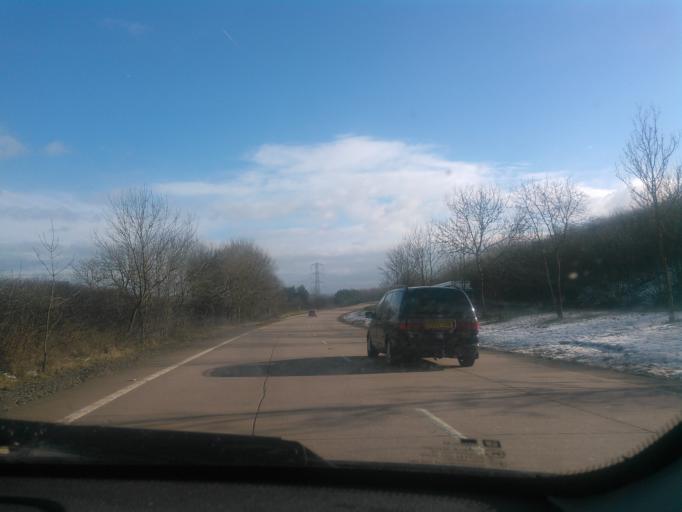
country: GB
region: England
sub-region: Staffordshire
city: Cheadle
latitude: 52.9328
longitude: -1.9599
